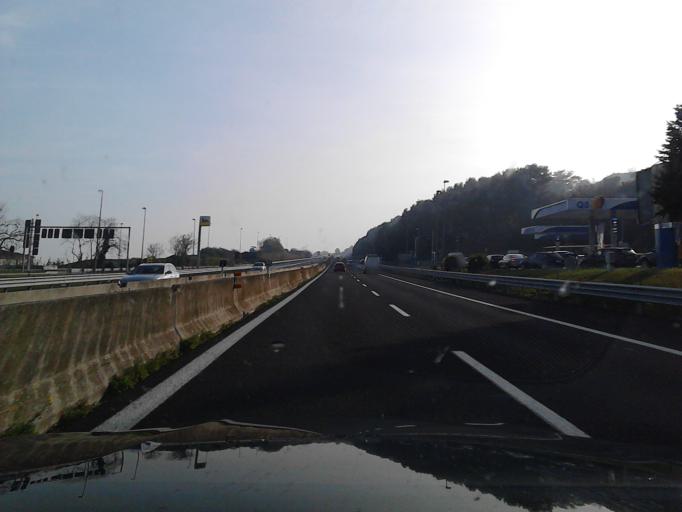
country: IT
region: The Marches
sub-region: Province of Fermo
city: Campofilone
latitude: 43.0751
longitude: 13.8435
